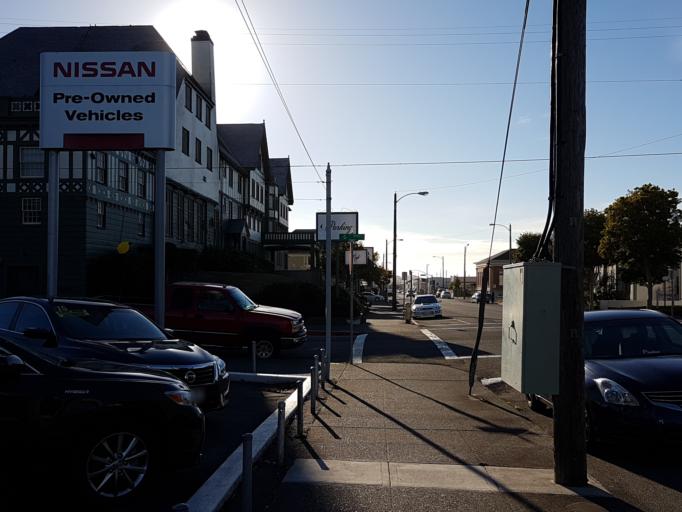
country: US
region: California
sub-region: Humboldt County
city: Eureka
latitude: 40.8004
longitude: -124.1642
